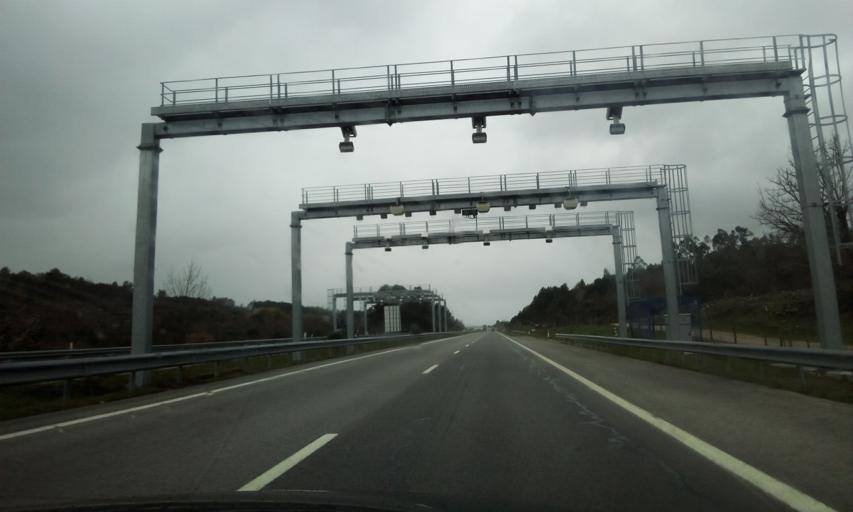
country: PT
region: Guarda
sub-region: Fornos de Algodres
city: Fornos de Algodres
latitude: 40.6136
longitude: -7.6495
